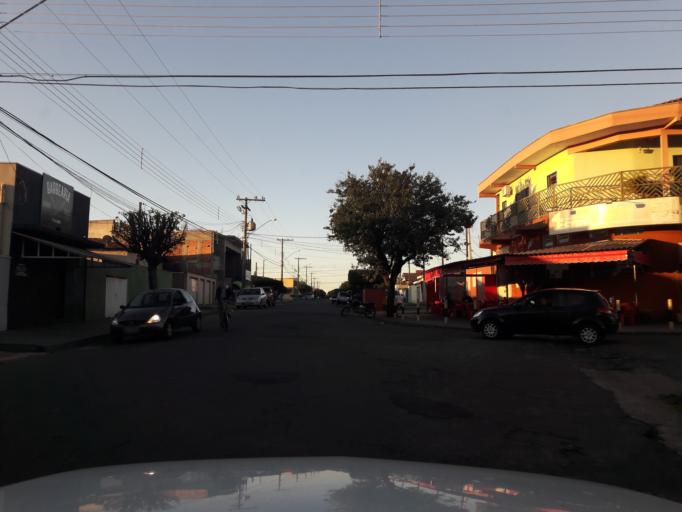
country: BR
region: Sao Paulo
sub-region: Moji-Guacu
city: Mogi-Gaucu
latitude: -22.3514
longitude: -46.9352
